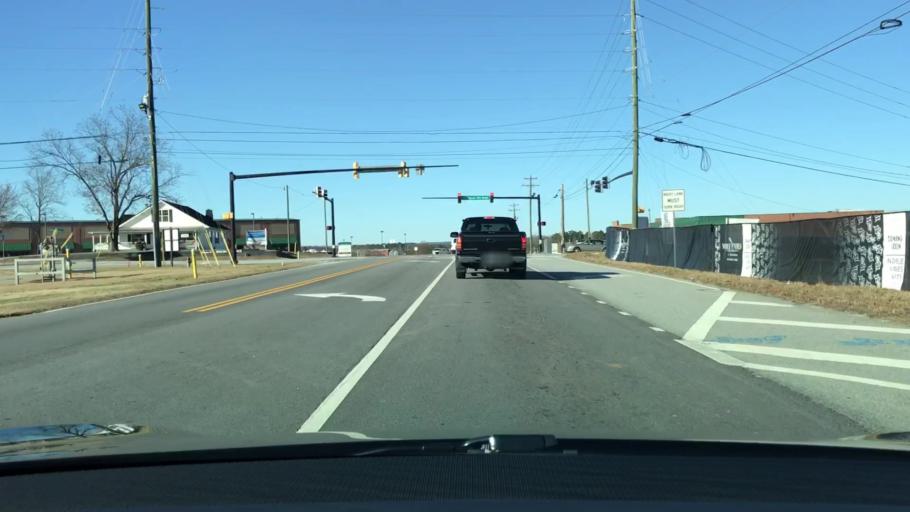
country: US
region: Georgia
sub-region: Hall County
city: Flowery Branch
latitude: 34.1051
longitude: -83.8726
